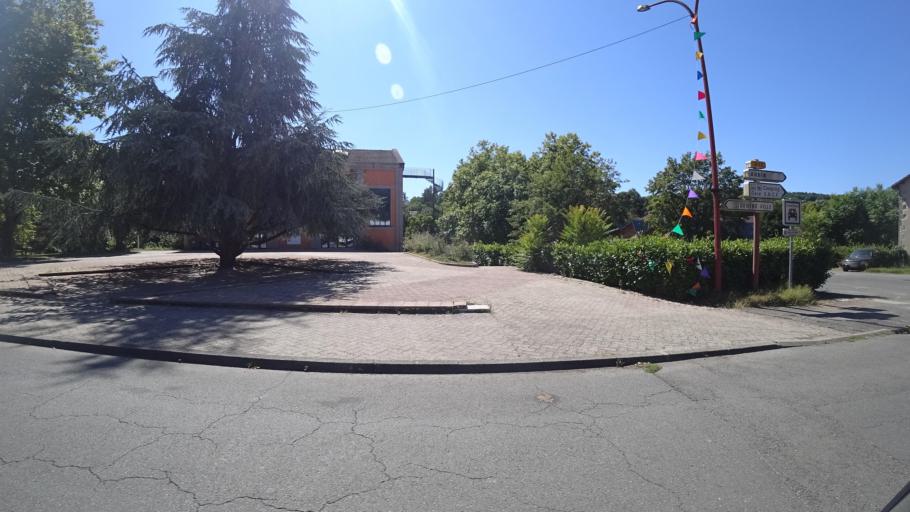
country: FR
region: Midi-Pyrenees
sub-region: Departement de l'Aveyron
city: Cransac
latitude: 44.5265
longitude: 2.2793
